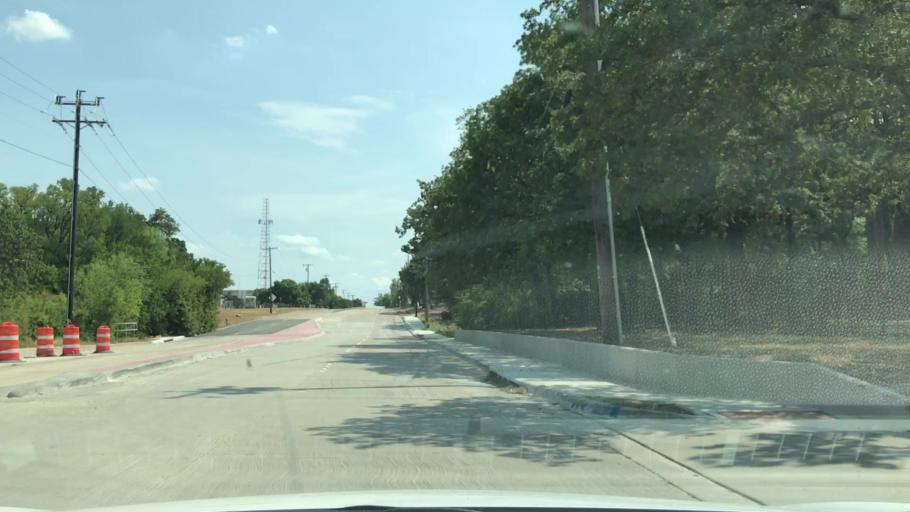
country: US
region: Texas
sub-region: Dallas County
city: Irving
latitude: 32.8355
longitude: -96.9075
